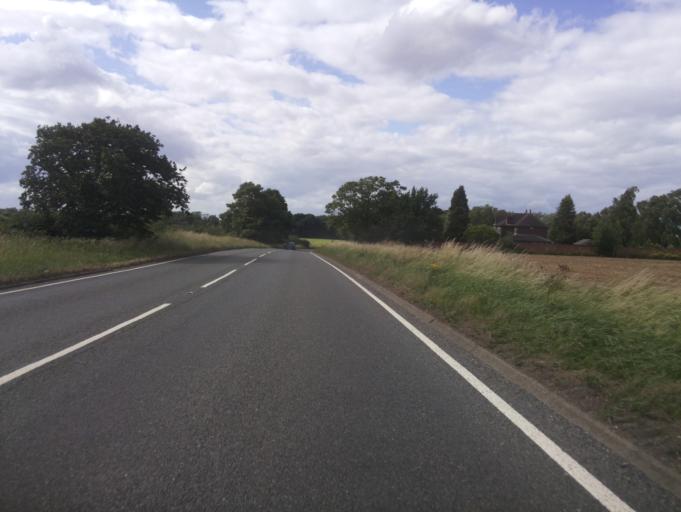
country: GB
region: England
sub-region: Leicestershire
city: Measham
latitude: 52.6713
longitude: -1.5406
